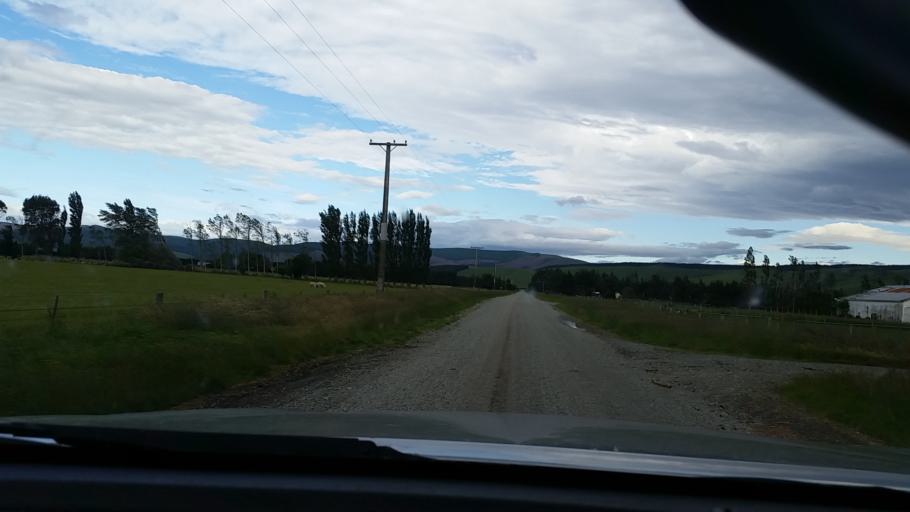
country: NZ
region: Southland
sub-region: Southland District
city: Winton
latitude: -45.8505
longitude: 168.3481
